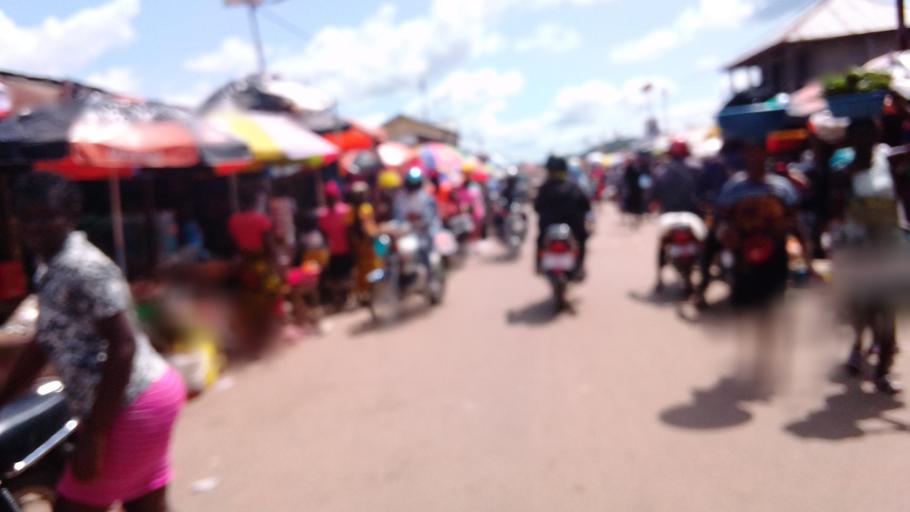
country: SL
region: Northern Province
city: Makeni
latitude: 8.8882
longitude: -12.0420
